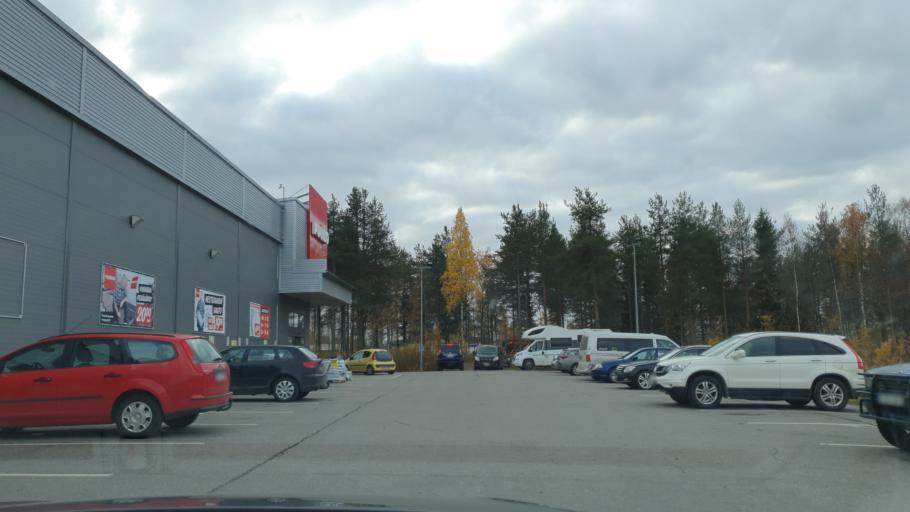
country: FI
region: Lapland
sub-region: Rovaniemi
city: Rovaniemi
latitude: 66.4898
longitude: 25.6696
